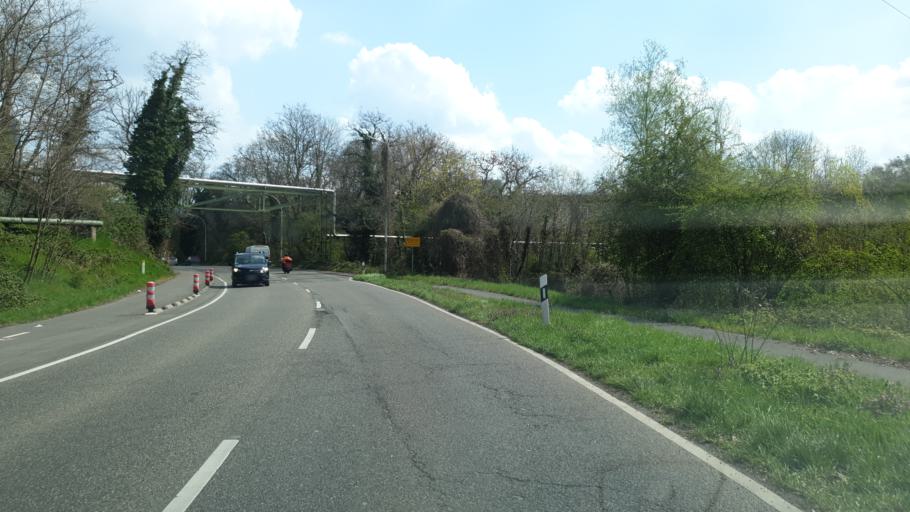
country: DE
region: North Rhine-Westphalia
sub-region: Regierungsbezirk Koln
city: Frechen
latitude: 50.9019
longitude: 6.7883
